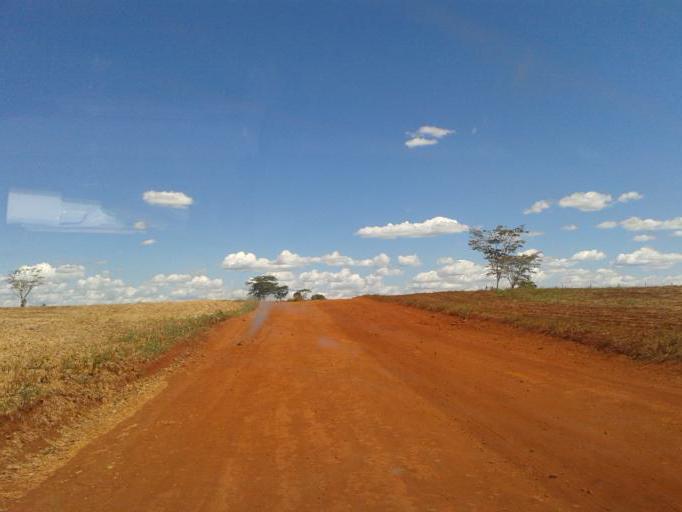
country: BR
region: Minas Gerais
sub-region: Capinopolis
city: Capinopolis
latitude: -18.6373
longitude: -49.5903
